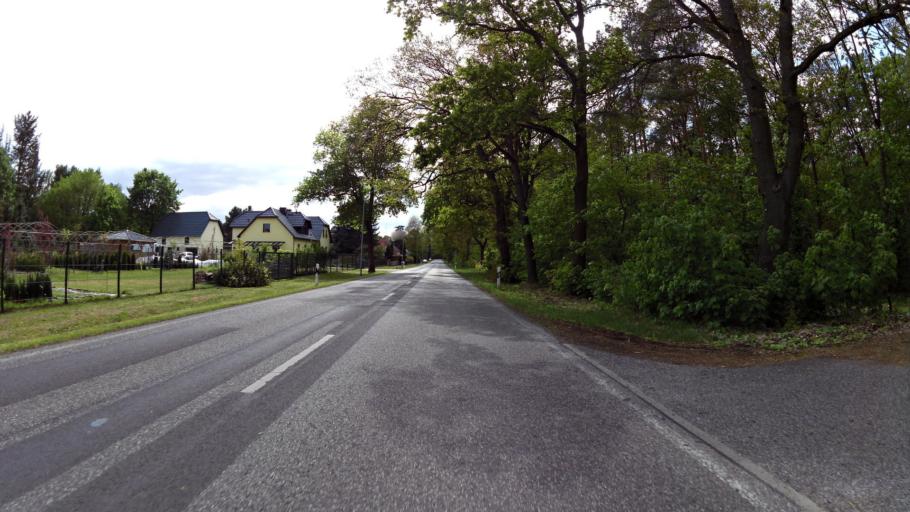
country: DE
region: Brandenburg
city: Rauen
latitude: 52.3563
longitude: 14.0195
